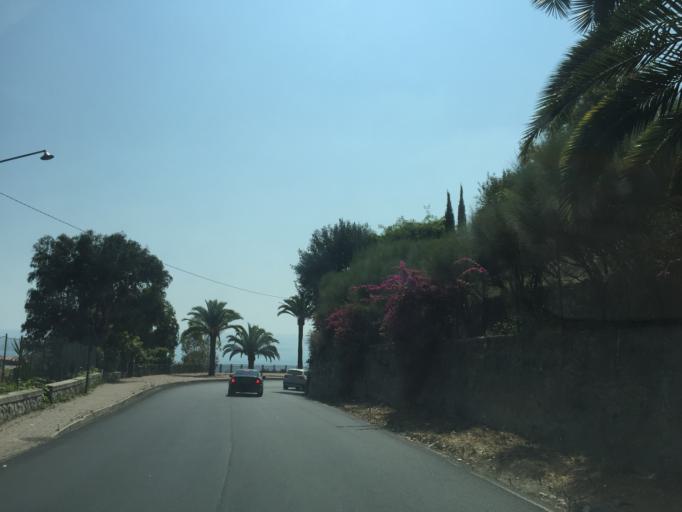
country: IT
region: Liguria
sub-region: Provincia di Imperia
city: Ventimiglia
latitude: 43.7935
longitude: 7.5796
